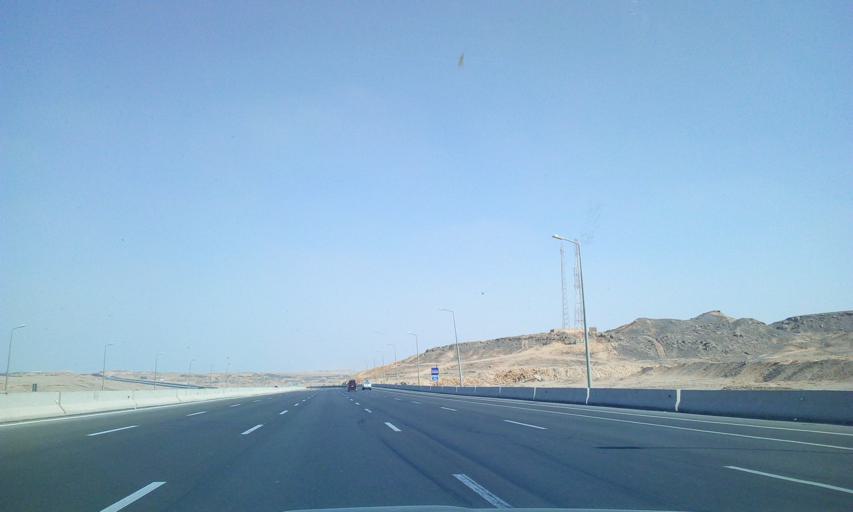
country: EG
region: As Suways
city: Ain Sukhna
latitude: 29.7011
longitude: 32.0969
